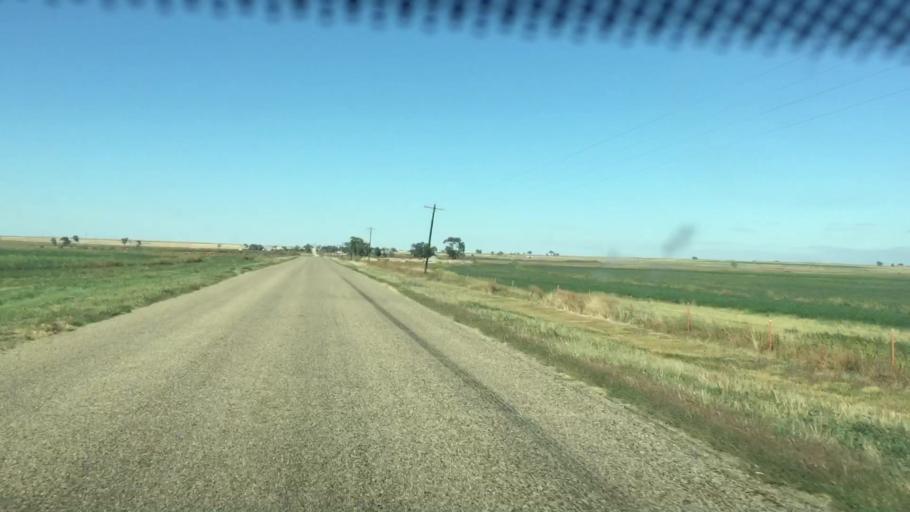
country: US
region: Colorado
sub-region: Prowers County
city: Lamar
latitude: 38.1035
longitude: -102.5215
